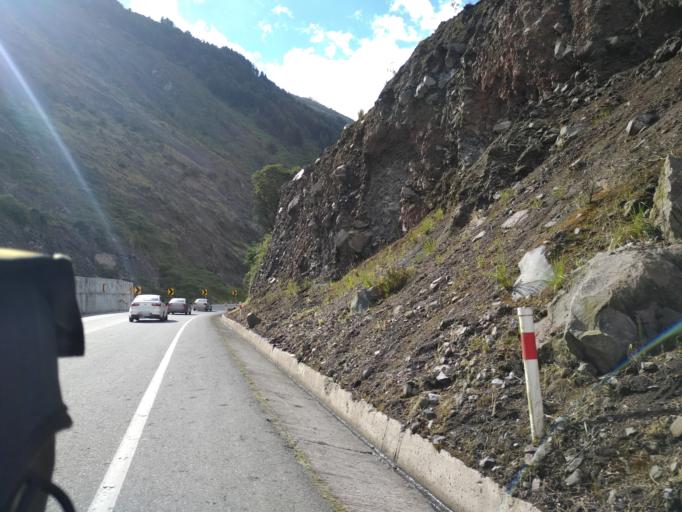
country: EC
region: Tungurahua
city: Banos
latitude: -1.4873
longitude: -78.5173
